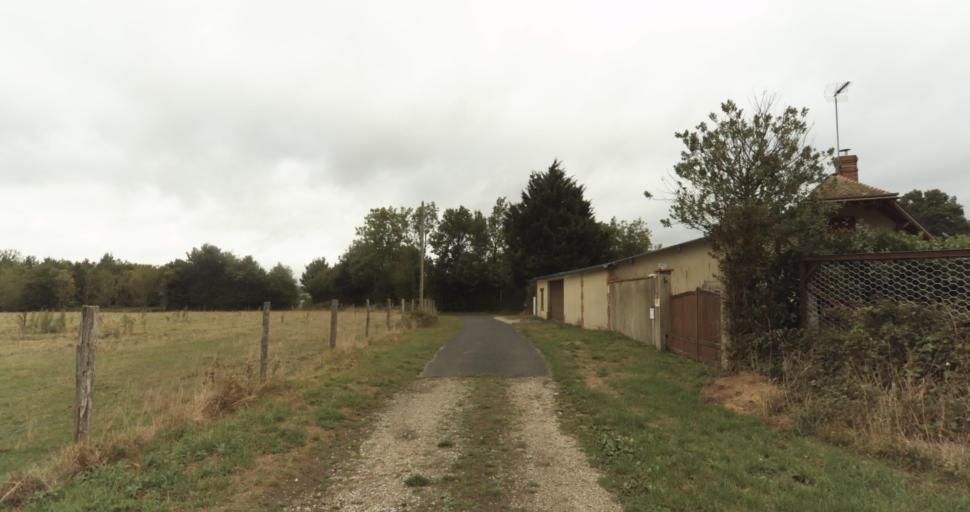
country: FR
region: Lower Normandy
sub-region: Departement de l'Orne
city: Sainte-Gauburge-Sainte-Colombe
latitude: 48.7169
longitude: 0.4470
